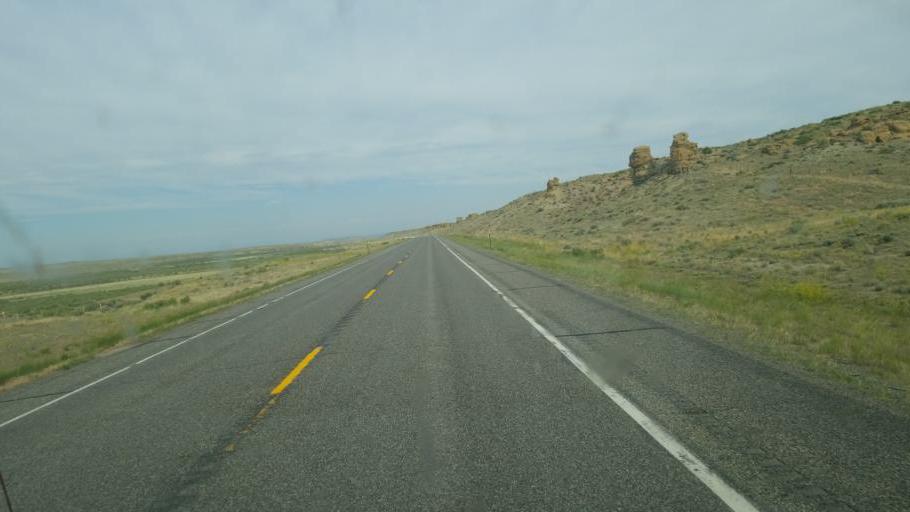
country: US
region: Wyoming
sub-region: Fremont County
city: Riverton
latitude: 43.2217
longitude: -108.0216
